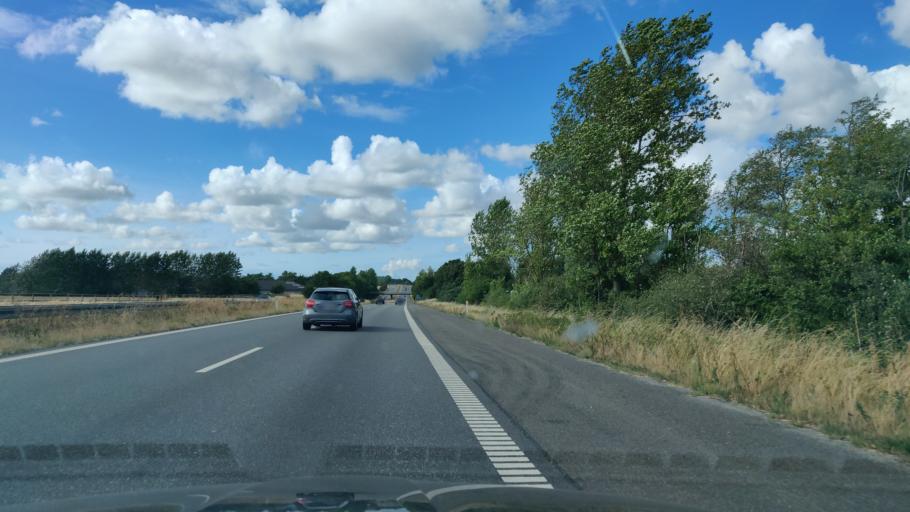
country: DK
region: Zealand
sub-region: Holbaek Kommune
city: Vipperod
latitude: 55.6579
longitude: 11.7636
